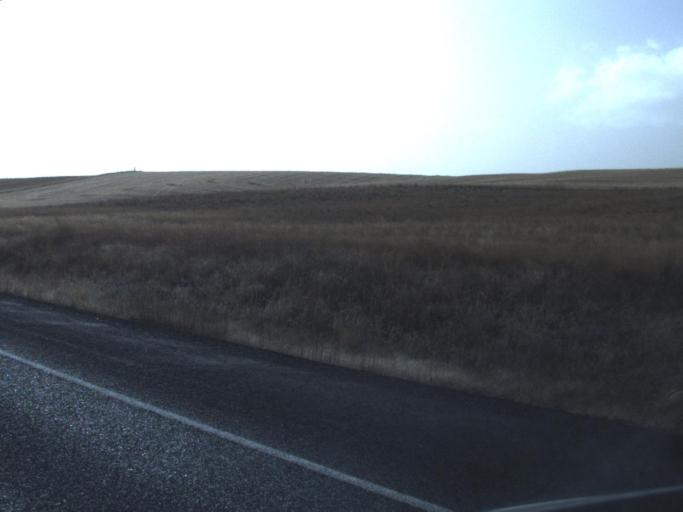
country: US
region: Washington
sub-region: Lincoln County
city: Davenport
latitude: 47.5397
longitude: -118.1955
